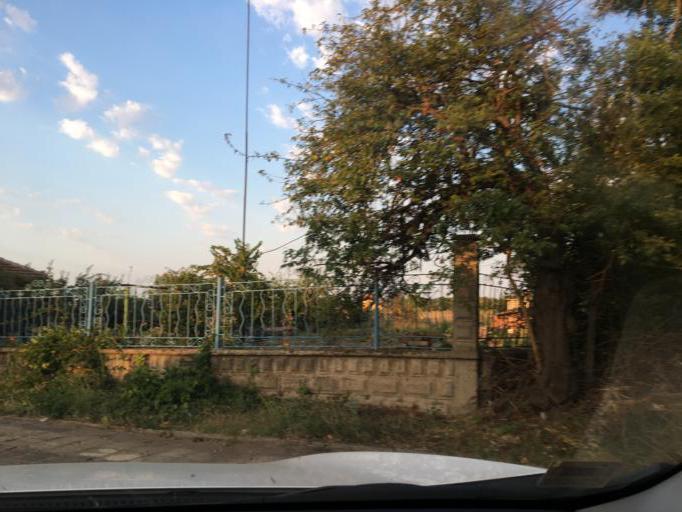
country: BG
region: Burgas
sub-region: Obshtina Burgas
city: Burgas
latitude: 42.6104
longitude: 27.4939
